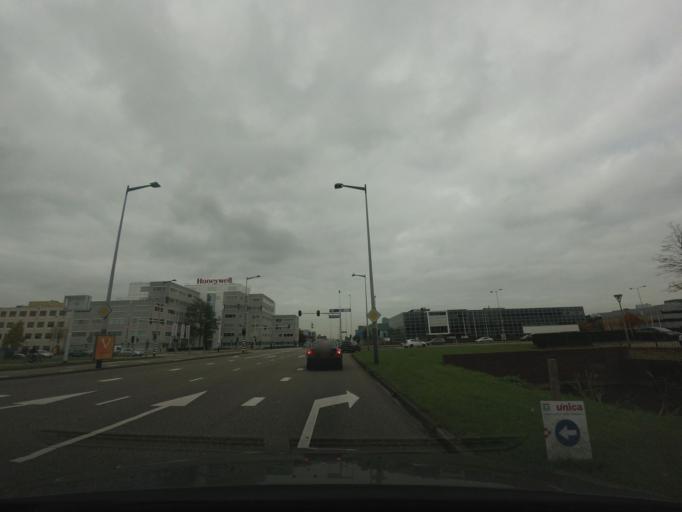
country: NL
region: North Holland
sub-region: Gemeente Amsterdam
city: Amsterdam-Zuidoost
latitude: 52.3017
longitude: 4.9455
